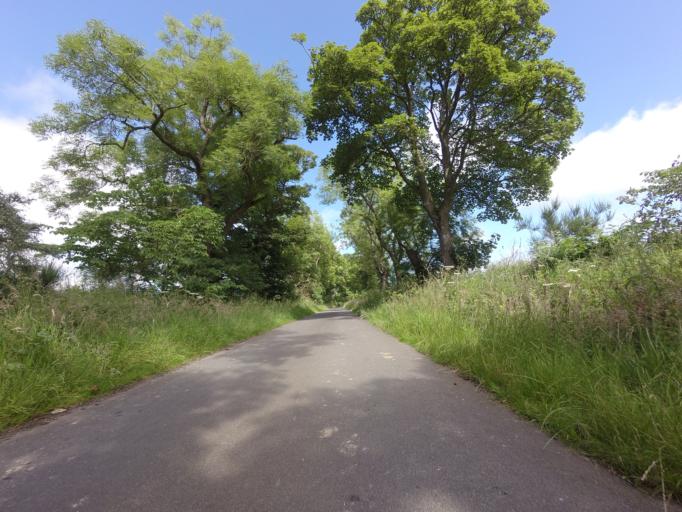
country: GB
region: Scotland
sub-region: Aberdeenshire
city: Turriff
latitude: 57.5894
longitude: -2.5046
